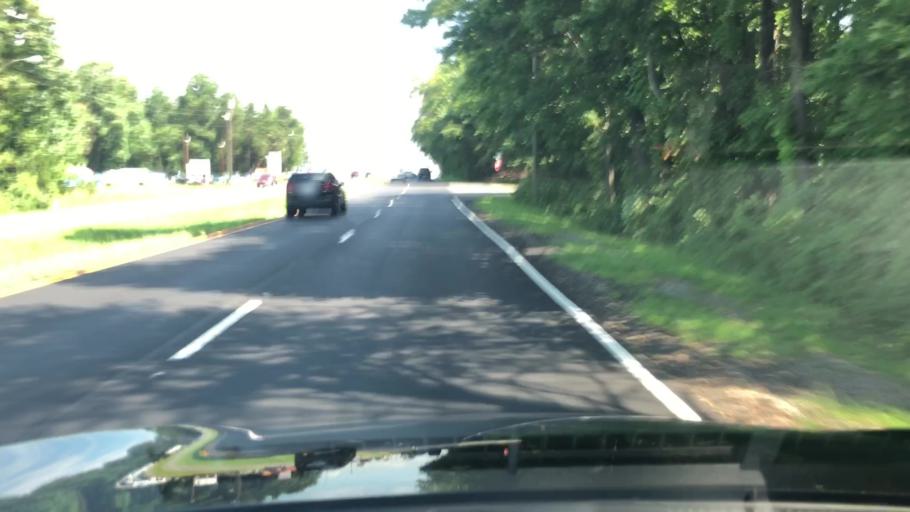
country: US
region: Virginia
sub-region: City of Fredericksburg
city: Fredericksburg
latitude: 38.2767
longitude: -77.4907
